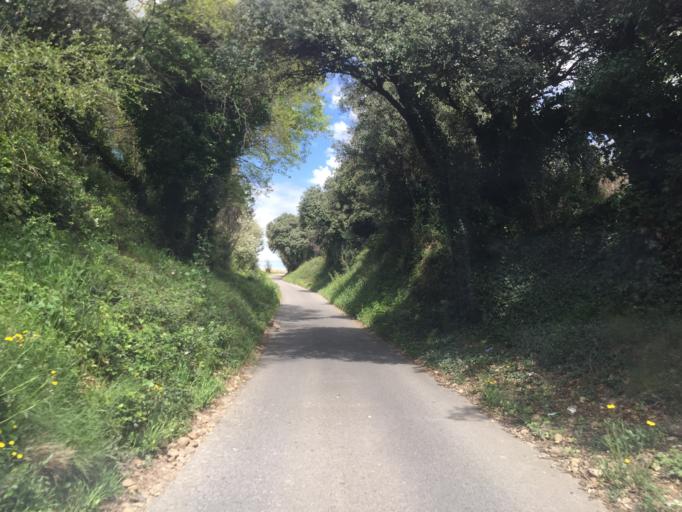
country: FR
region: Provence-Alpes-Cote d'Azur
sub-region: Departement du Vaucluse
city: Chateauneuf-du-Pape
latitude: 44.0638
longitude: 4.8330
